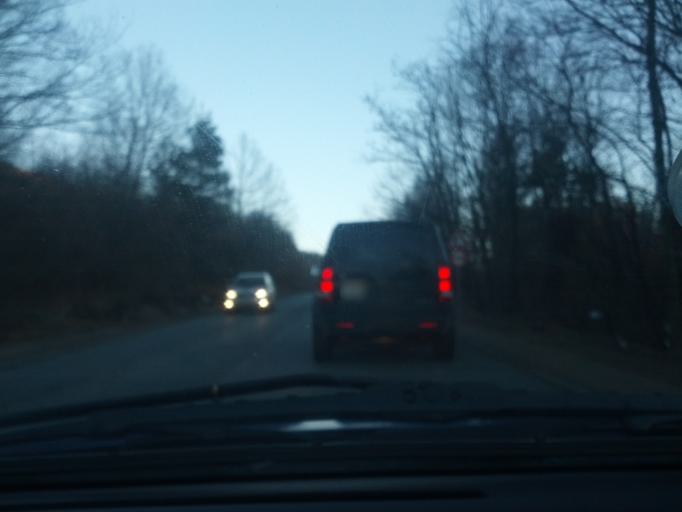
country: BG
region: Vratsa
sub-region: Obshtina Mezdra
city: Mezdra
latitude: 43.0228
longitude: 23.6762
